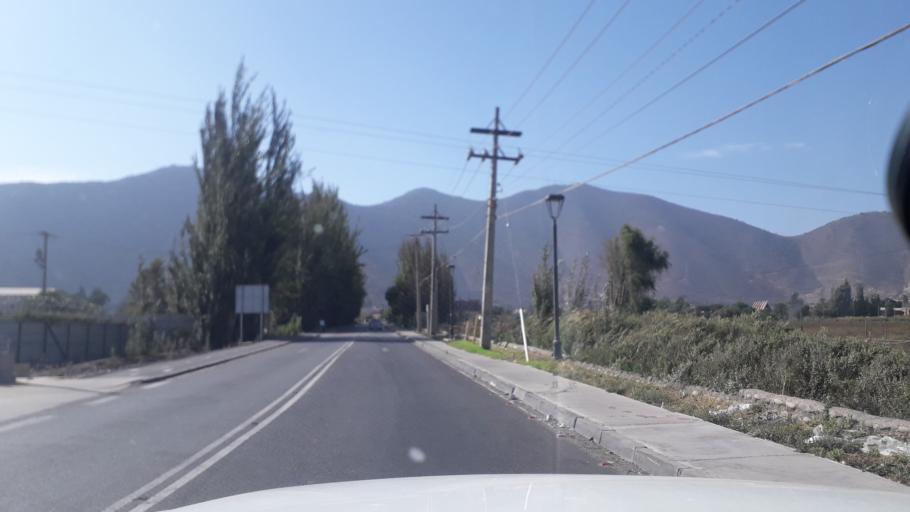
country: CL
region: Valparaiso
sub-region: Provincia de San Felipe
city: Llaillay
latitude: -32.8463
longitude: -70.9600
